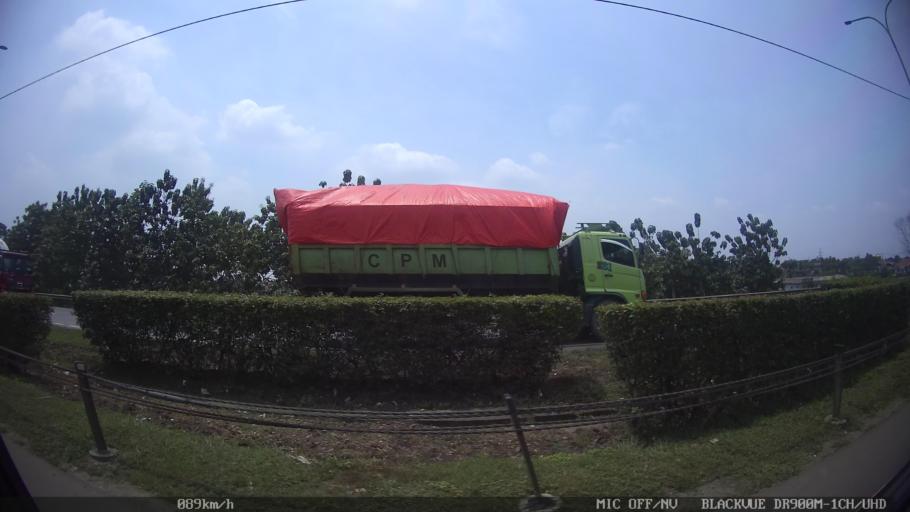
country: ID
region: West Java
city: Kresek
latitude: -6.1524
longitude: 106.3159
